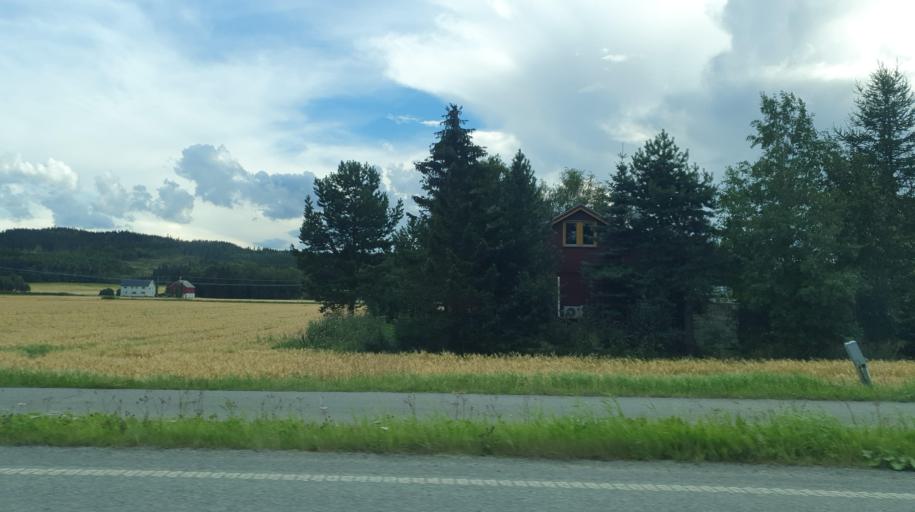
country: NO
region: Nord-Trondelag
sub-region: Levanger
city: Levanger
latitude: 63.7540
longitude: 11.3723
